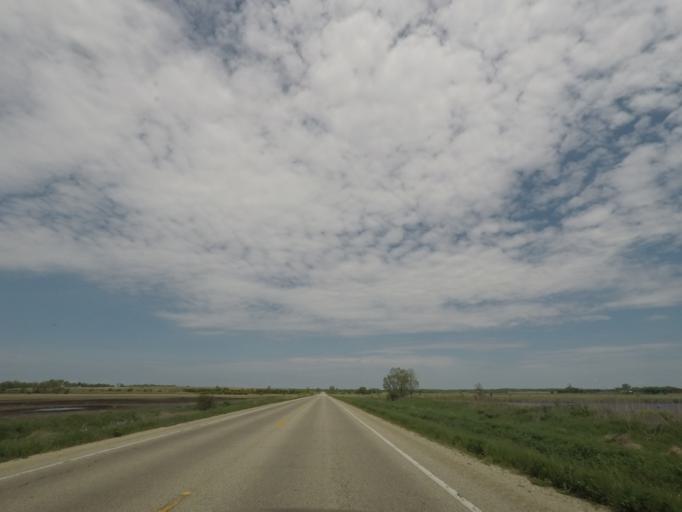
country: US
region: Wisconsin
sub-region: Rock County
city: Evansville
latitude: 42.7457
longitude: -89.2989
